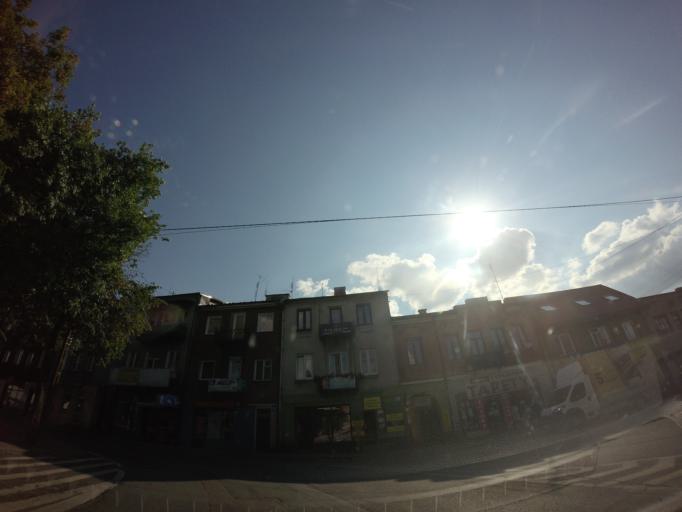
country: PL
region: Masovian Voivodeship
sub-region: Powiat sokolowski
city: Sokolow Podlaski
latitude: 52.4063
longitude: 22.2532
